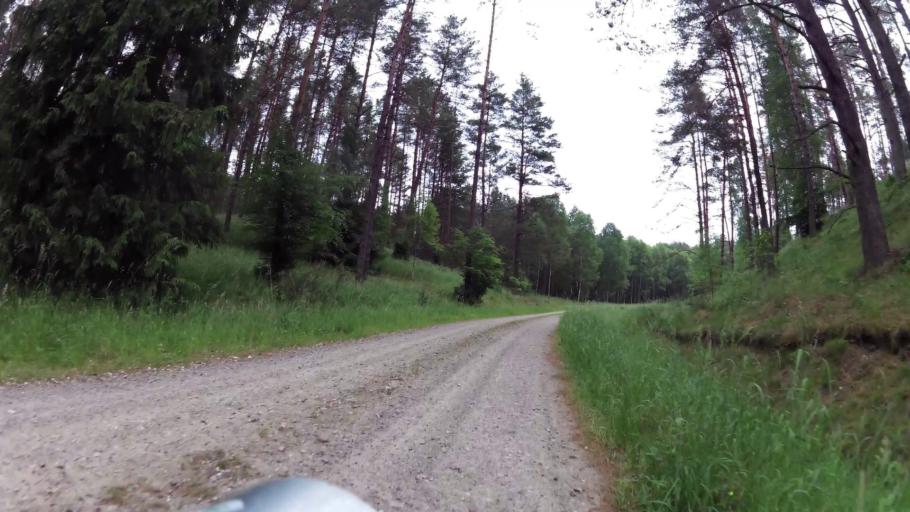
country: PL
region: West Pomeranian Voivodeship
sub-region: Powiat szczecinecki
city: Bialy Bor
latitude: 53.9507
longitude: 16.8298
